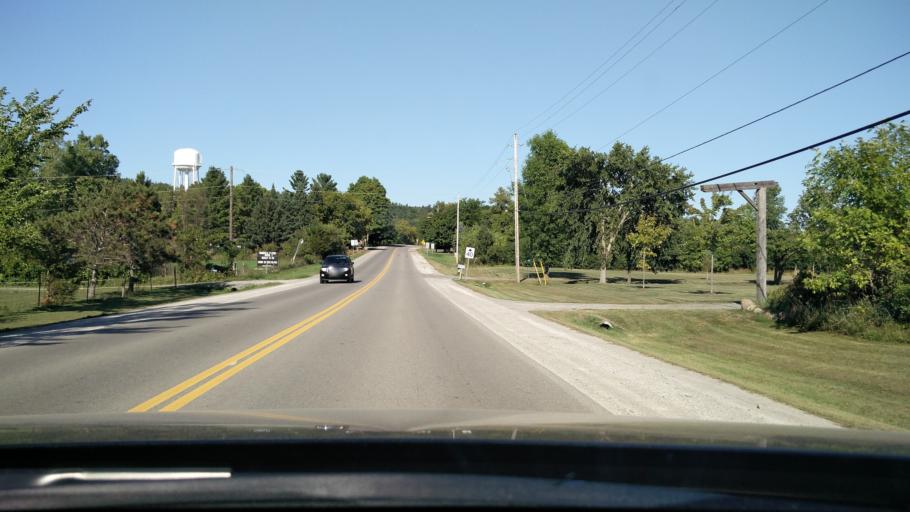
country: CA
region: Ontario
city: Perth
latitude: 44.6785
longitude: -76.4115
